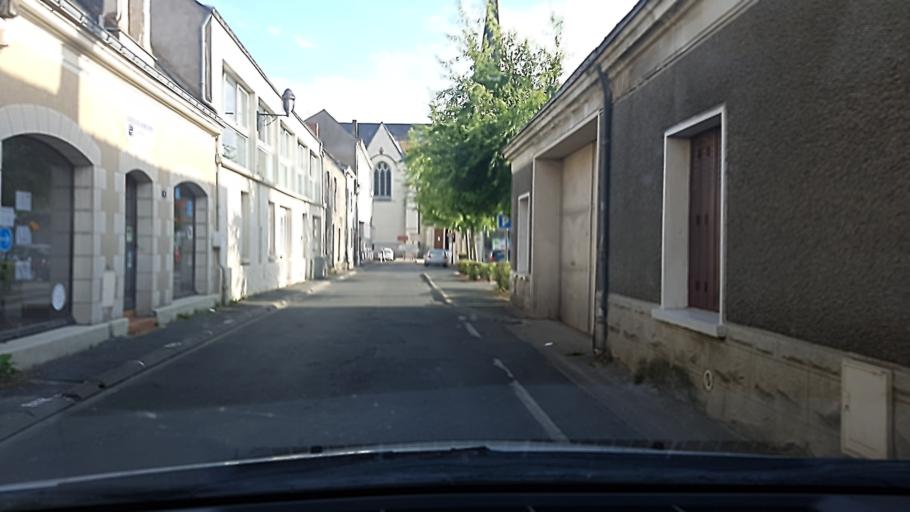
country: FR
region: Pays de la Loire
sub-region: Departement de Maine-et-Loire
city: Maze
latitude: 47.4569
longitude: -0.2719
